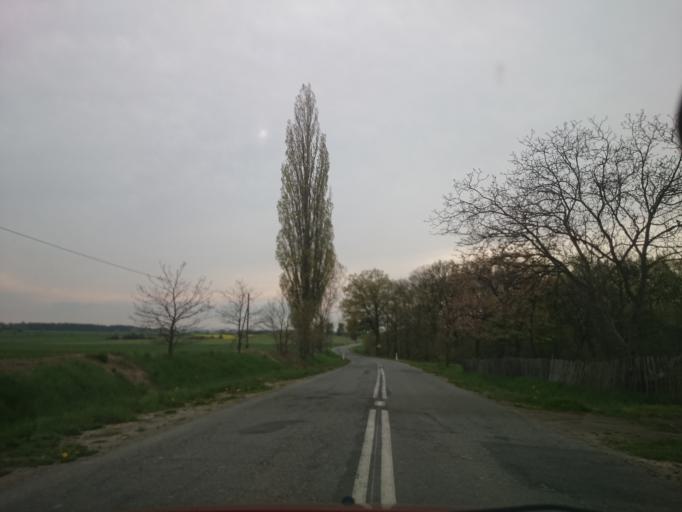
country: PL
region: Lower Silesian Voivodeship
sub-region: Powiat strzelinski
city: Przeworno
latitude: 50.6446
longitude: 17.2126
